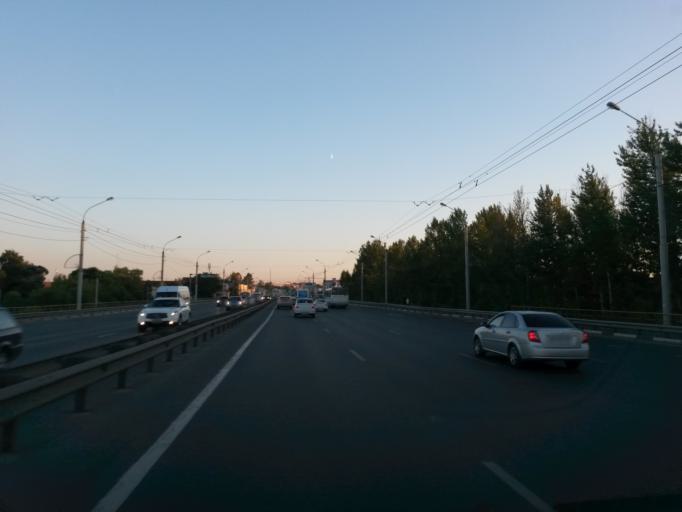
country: RU
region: Jaroslavl
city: Yaroslavl
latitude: 57.6171
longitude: 39.8849
